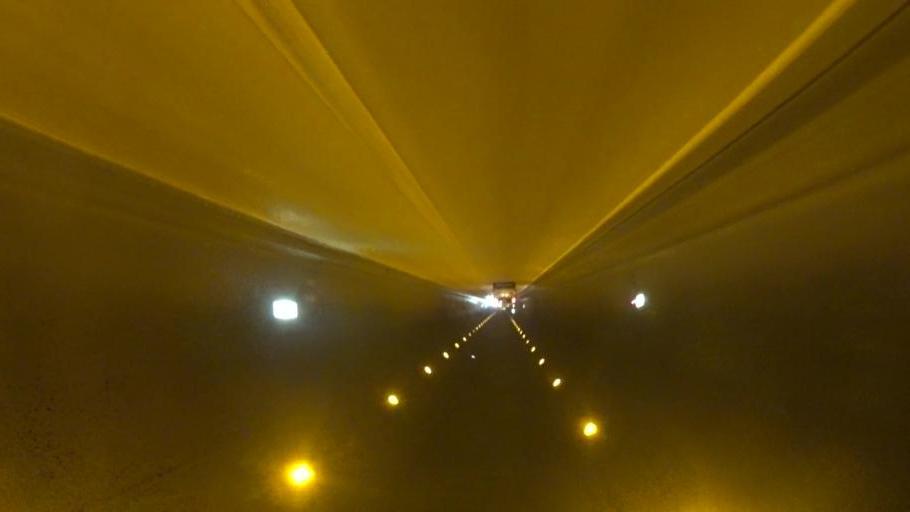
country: JP
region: Kyoto
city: Miyazu
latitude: 35.5476
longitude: 135.1808
